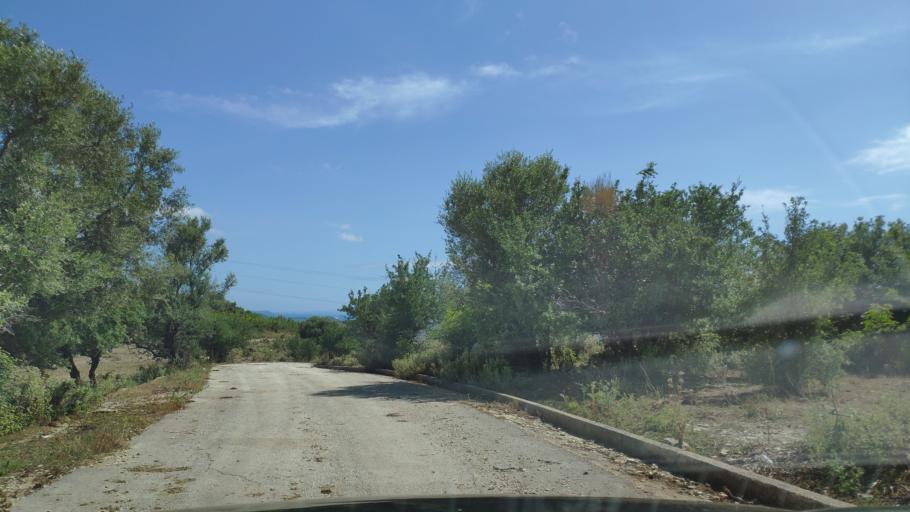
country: AL
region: Vlore
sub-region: Rrethi i Sarandes
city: Konispol
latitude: 39.6289
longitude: 20.2102
